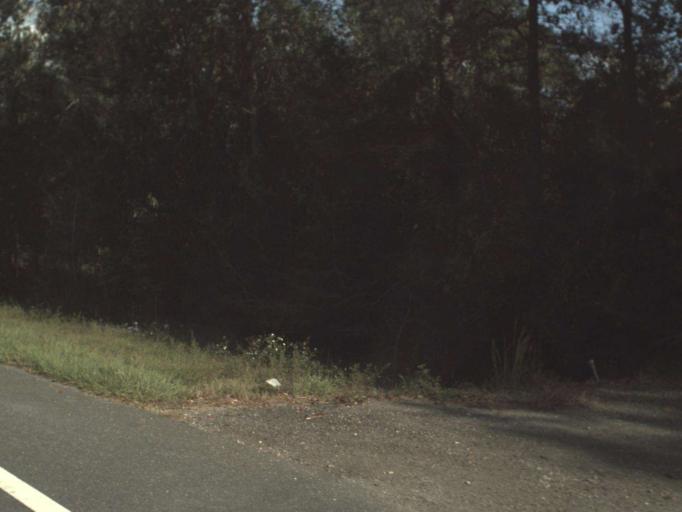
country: US
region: Florida
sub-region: Holmes County
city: Bonifay
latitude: 30.6556
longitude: -85.6641
